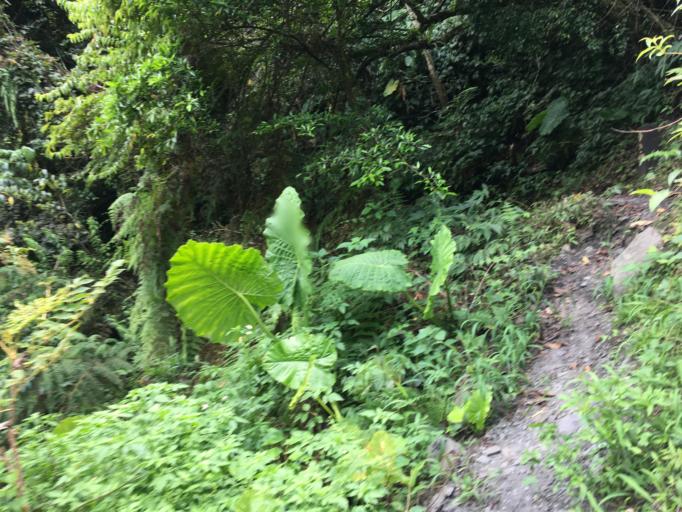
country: TW
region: Taiwan
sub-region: Yilan
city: Yilan
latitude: 24.4229
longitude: 121.6951
